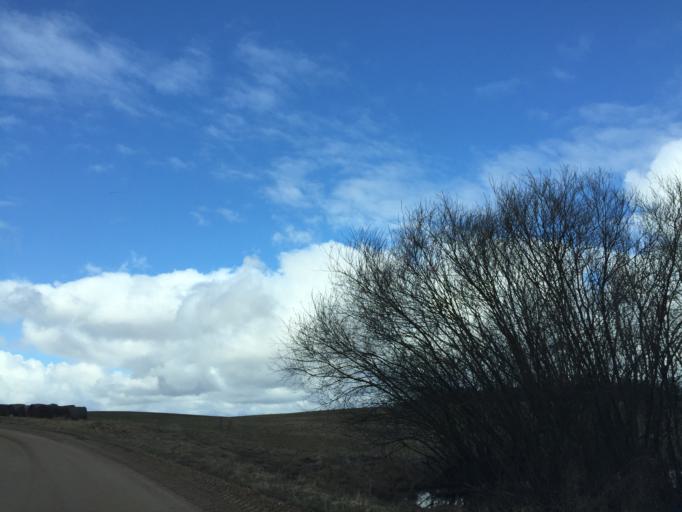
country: LV
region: Akniste
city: Akniste
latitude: 56.0925
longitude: 26.0050
